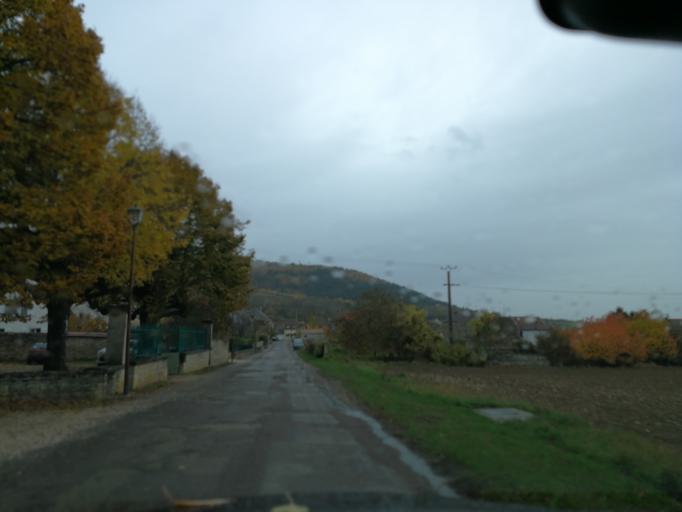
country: FR
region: Bourgogne
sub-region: Departement de la Cote-d'Or
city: Fleurey-sur-Ouche
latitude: 47.3252
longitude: 4.7969
